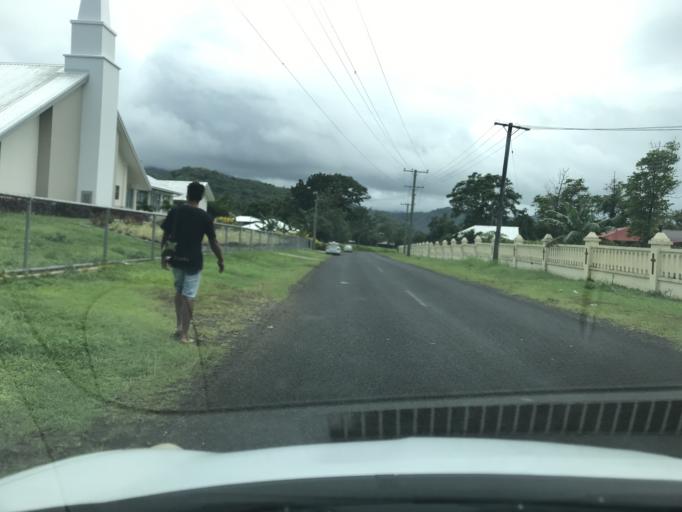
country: WS
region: Atua
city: Lufilufi
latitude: -13.8753
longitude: -171.5983
